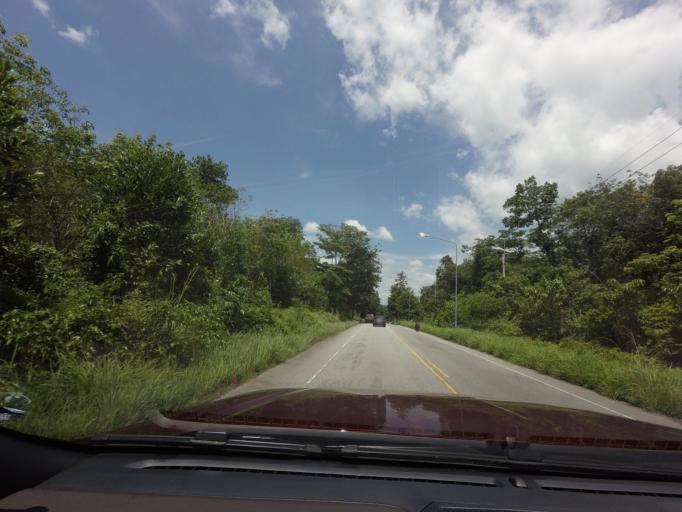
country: TH
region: Narathiwat
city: Ra-ngae
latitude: 6.2031
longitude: 101.6875
